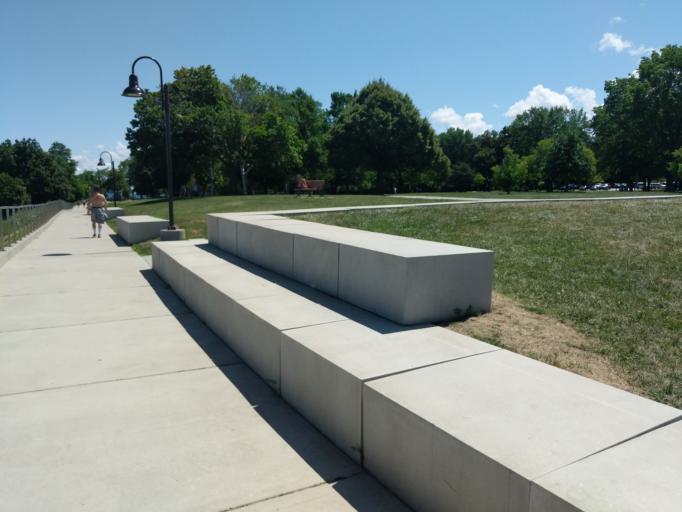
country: US
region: Ohio
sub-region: Cuyahoga County
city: Lakewood
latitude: 41.4972
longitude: -81.7976
